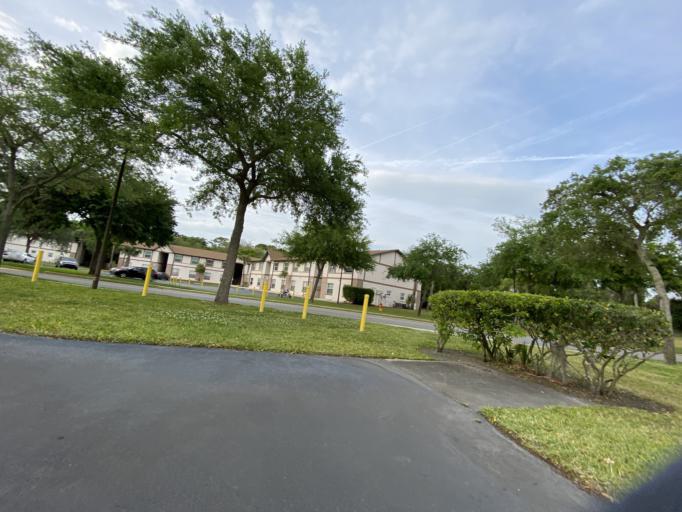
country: US
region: Florida
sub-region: Volusia County
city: South Daytona
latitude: 29.1600
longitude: -80.9979
